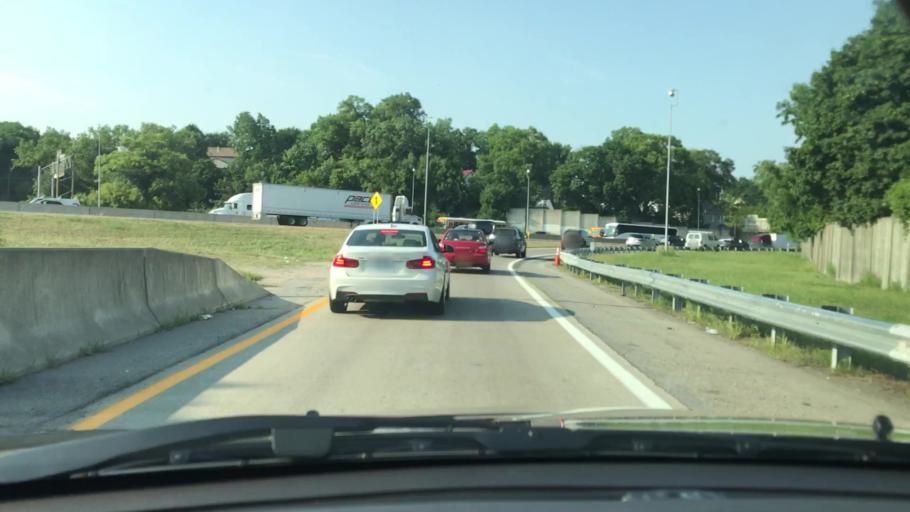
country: US
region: New York
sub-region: Westchester County
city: Mamaroneck
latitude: 40.9617
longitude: -73.7347
